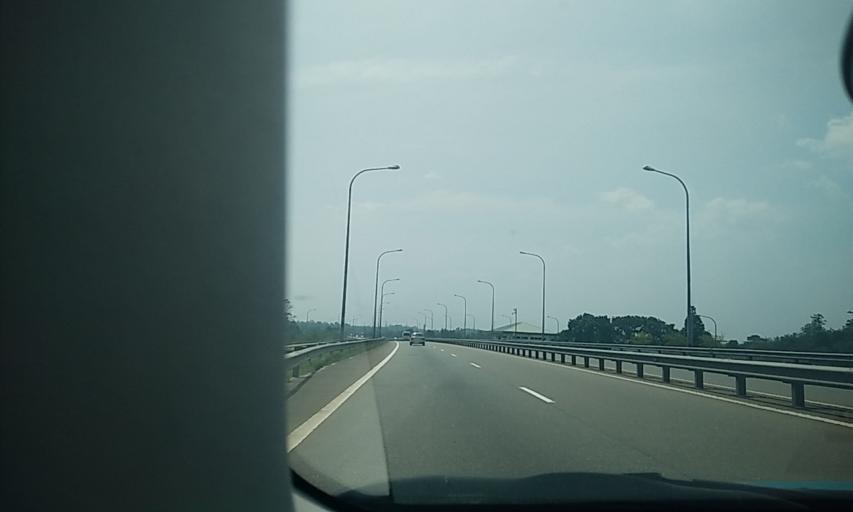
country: LK
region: Western
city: Homagama
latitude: 6.7840
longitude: 79.9804
